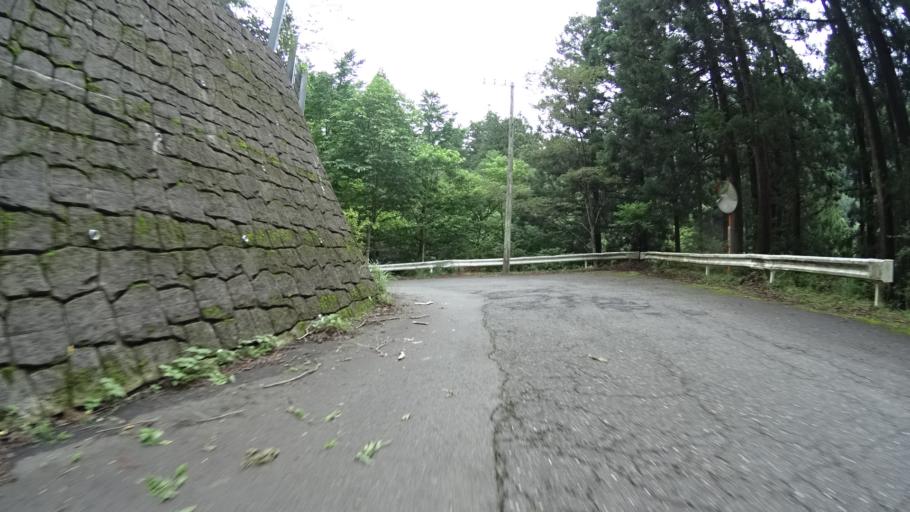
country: JP
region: Kanagawa
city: Hadano
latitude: 35.4688
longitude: 139.2171
